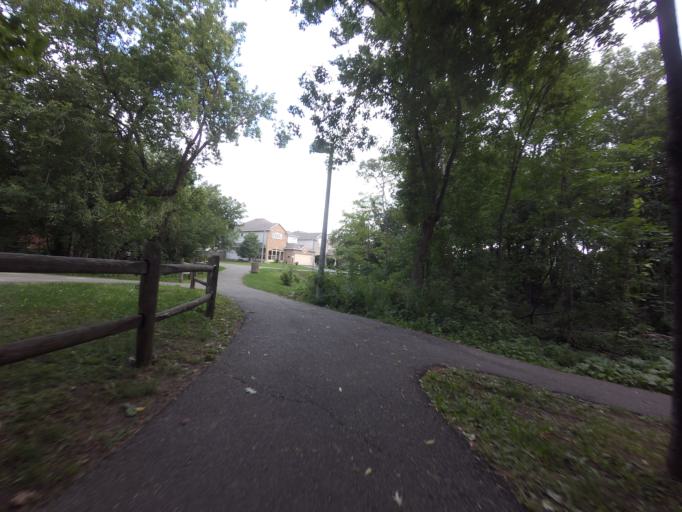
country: CA
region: Ontario
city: Bells Corners
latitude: 45.2834
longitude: -75.7322
